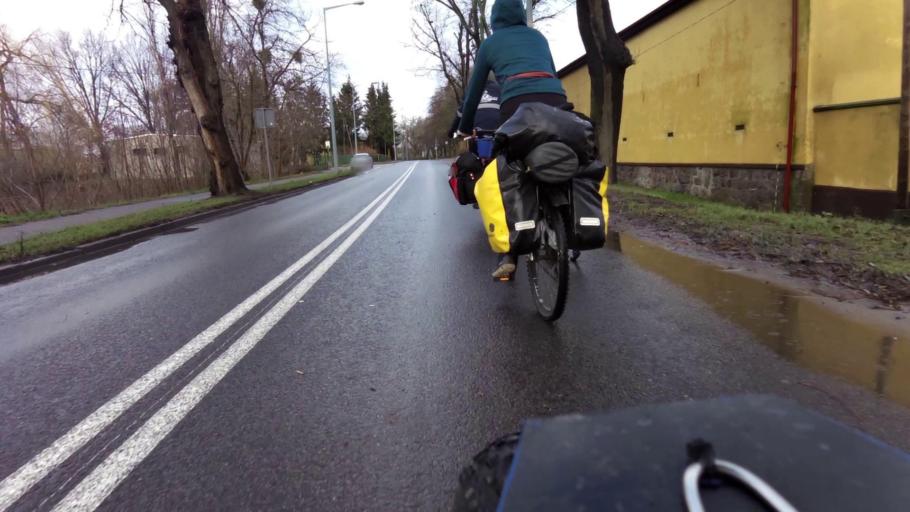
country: PL
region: Lubusz
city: Gorzow Wielkopolski
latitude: 52.7403
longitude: 15.1723
